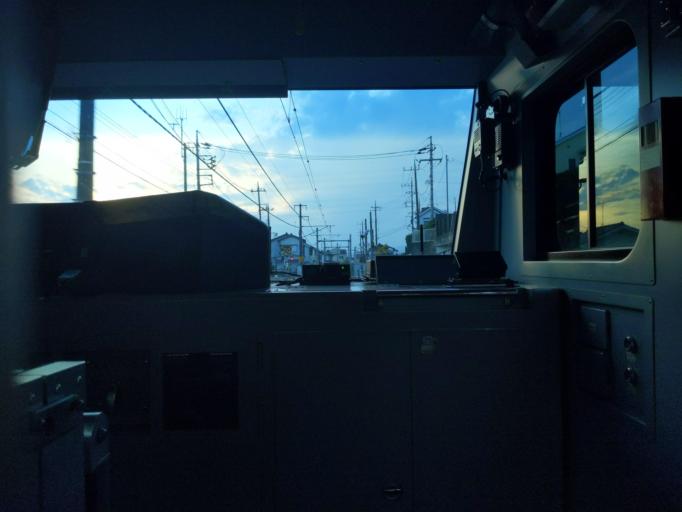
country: JP
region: Tokyo
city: Fussa
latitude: 35.7259
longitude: 139.3054
